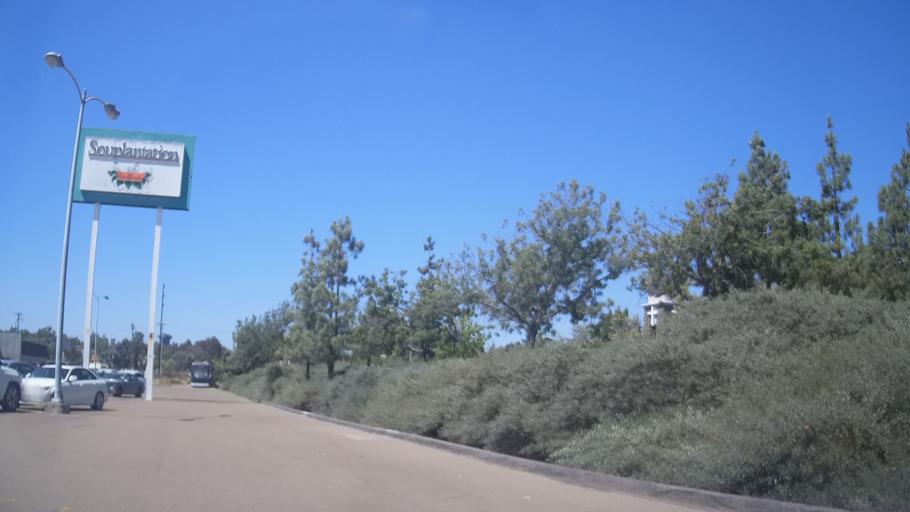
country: US
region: California
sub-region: San Diego County
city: La Mesa
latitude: 32.7934
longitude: -117.0024
